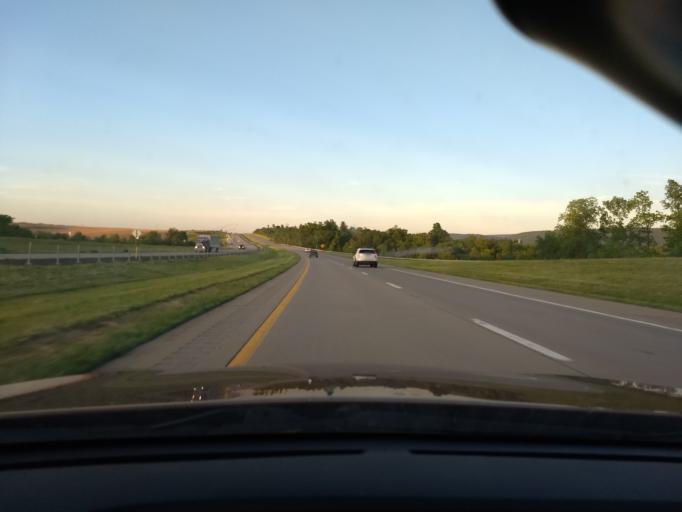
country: US
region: Pennsylvania
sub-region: Centre County
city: Houserville
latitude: 40.8470
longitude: -77.8107
